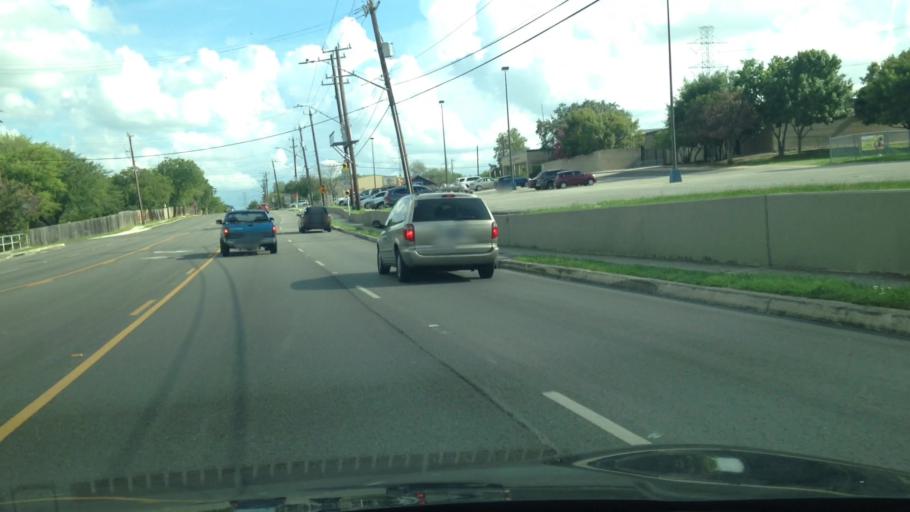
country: US
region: Texas
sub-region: Bexar County
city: Windcrest
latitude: 29.5693
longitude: -98.3953
